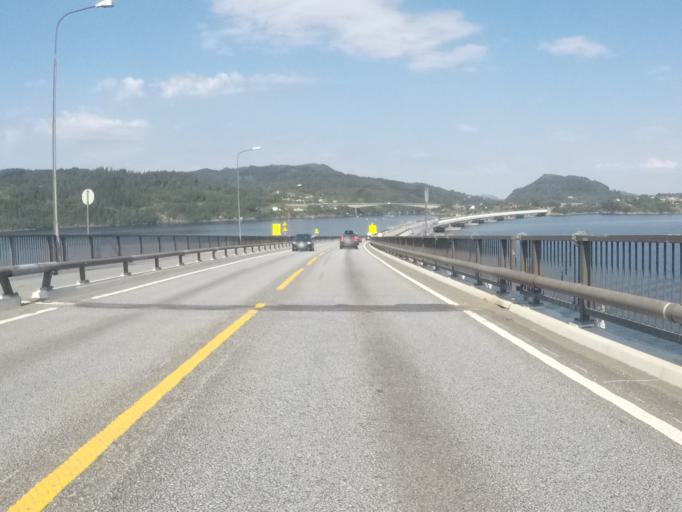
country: NO
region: Hordaland
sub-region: Lindas
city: Knarvik
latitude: 60.5215
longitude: 5.2697
